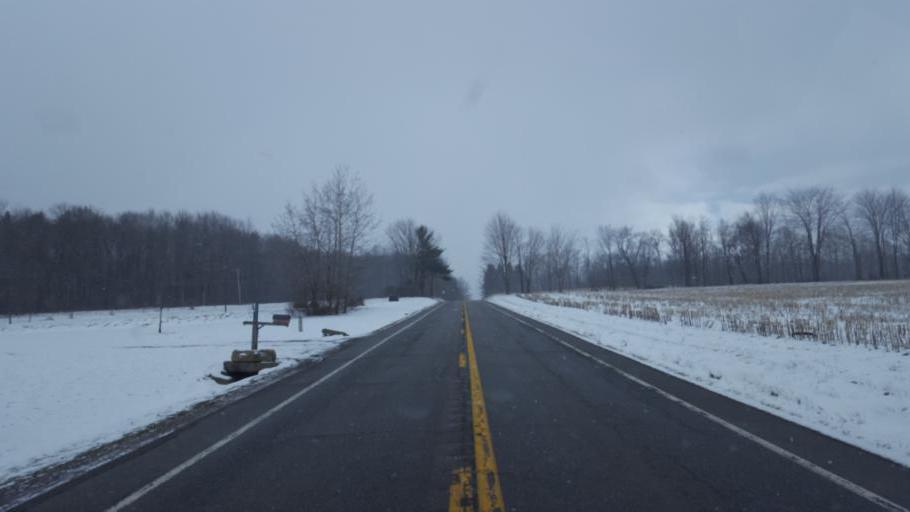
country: US
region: Pennsylvania
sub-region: Crawford County
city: Cochranton
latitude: 41.4362
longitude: -80.0747
